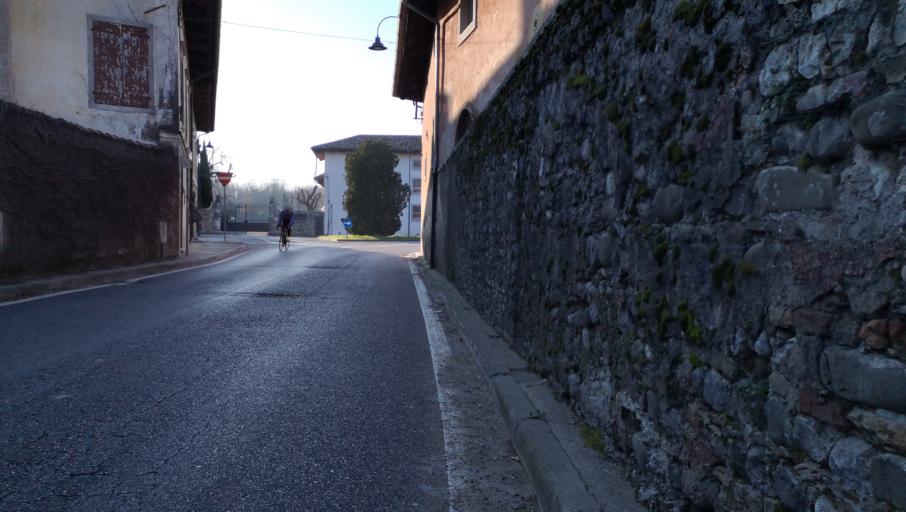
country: IT
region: Friuli Venezia Giulia
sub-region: Provincia di Udine
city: Lauzacco
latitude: 45.9659
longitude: 13.2964
